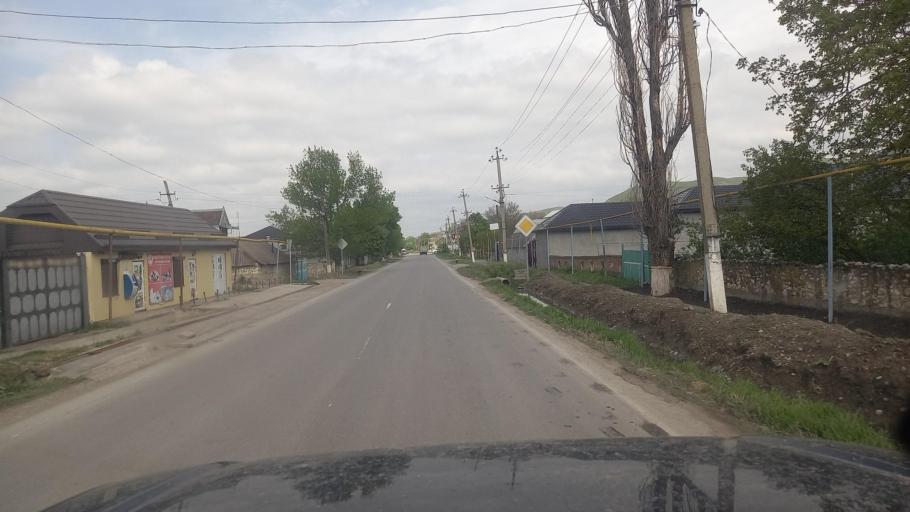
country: RU
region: Kabardino-Balkariya
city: Sarmakovo
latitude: 43.7457
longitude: 43.2051
